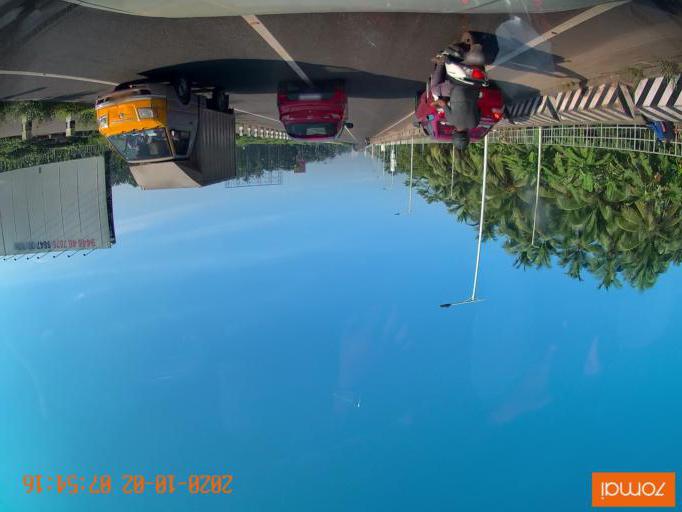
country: IN
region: Kerala
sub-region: Kozhikode
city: Ferokh
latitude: 11.1709
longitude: 75.8747
